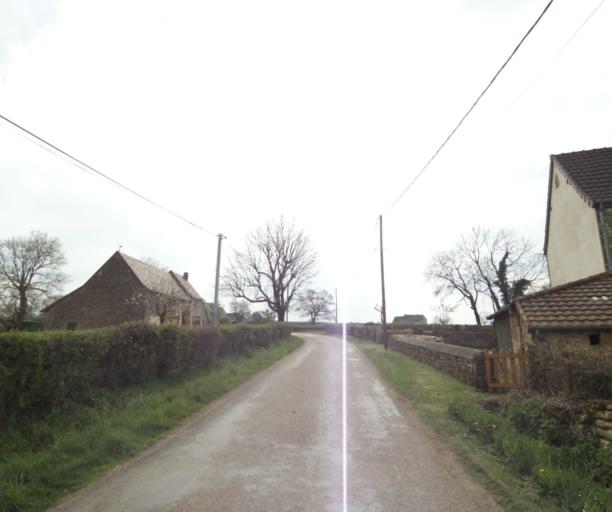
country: FR
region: Bourgogne
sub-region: Departement de Saone-et-Loire
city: Charolles
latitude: 46.3586
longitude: 4.2202
